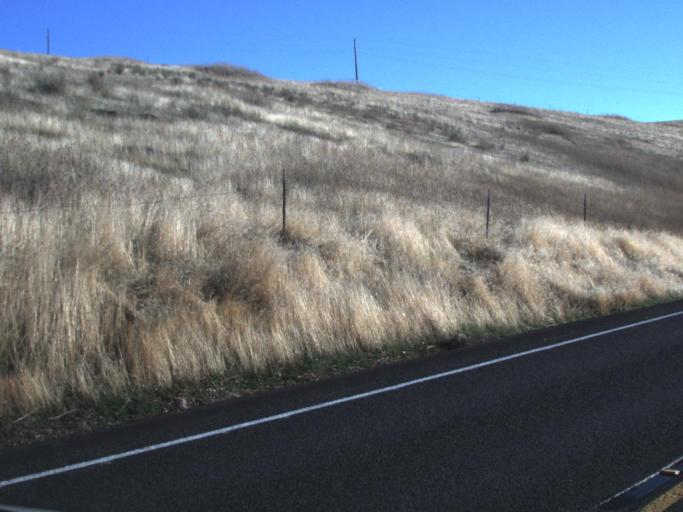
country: US
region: Washington
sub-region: Garfield County
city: Pomeroy
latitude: 46.5209
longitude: -117.8021
